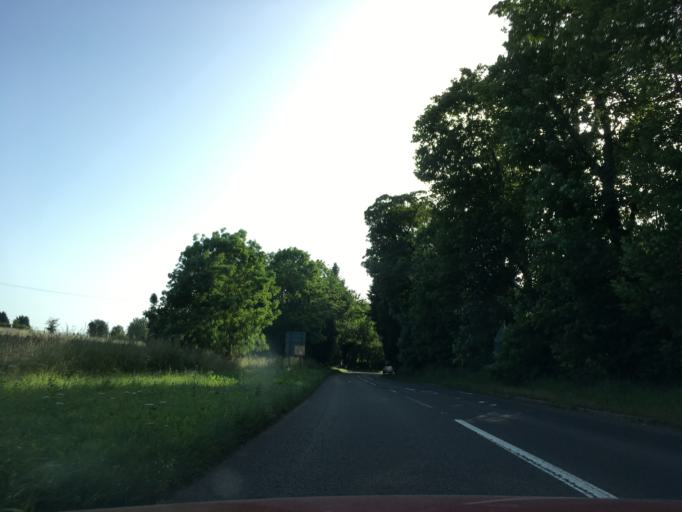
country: GB
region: England
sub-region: Gloucestershire
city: Cirencester
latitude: 51.7142
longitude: -1.9066
